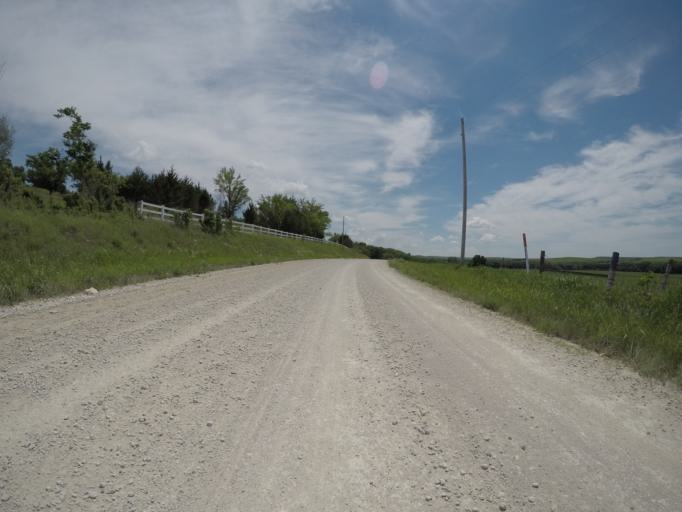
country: US
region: Kansas
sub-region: Wabaunsee County
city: Alma
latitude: 38.9423
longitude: -96.2367
